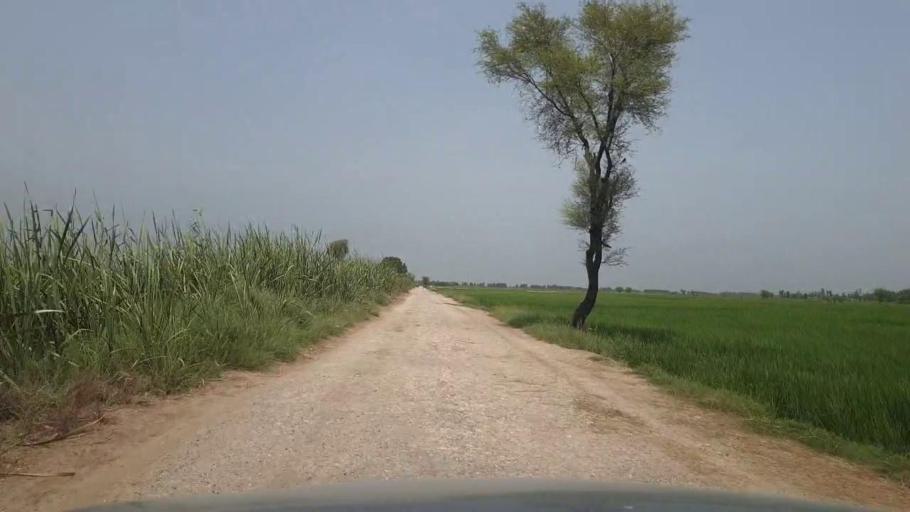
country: PK
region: Sindh
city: Garhi Yasin
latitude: 27.9350
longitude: 68.4317
